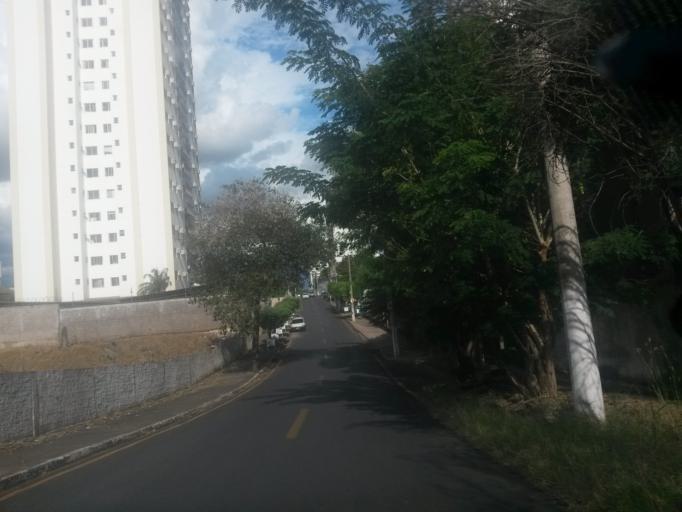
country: BR
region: Mato Grosso
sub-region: Cuiaba
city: Cuiaba
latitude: -15.6062
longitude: -56.0775
